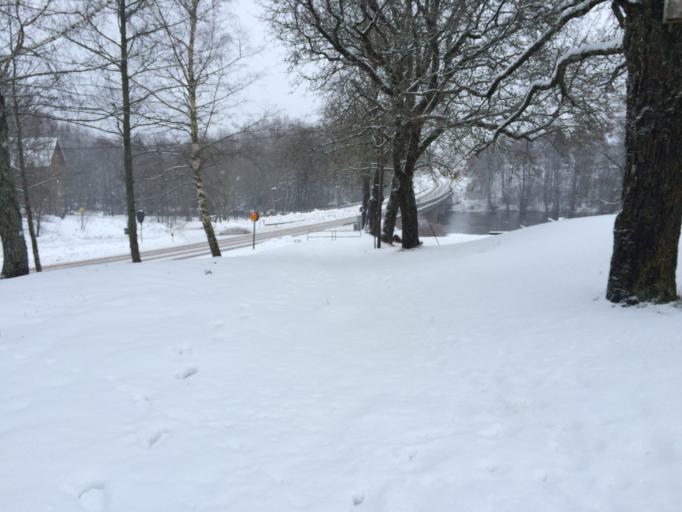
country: SE
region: Vaestmanland
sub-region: Hallstahammars Kommun
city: Hallstahammar
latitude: 59.6096
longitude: 16.2198
